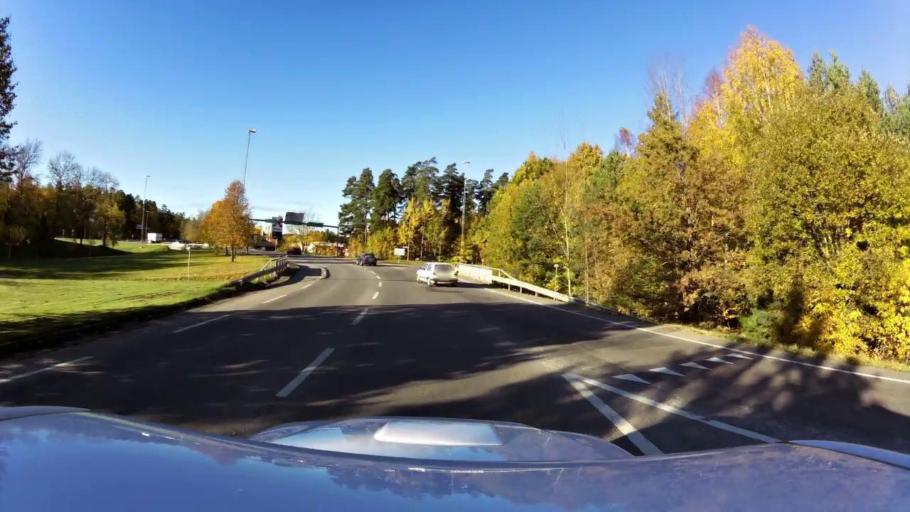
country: SE
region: OEstergoetland
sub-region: Linkopings Kommun
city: Linkoping
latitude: 58.4072
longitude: 15.5828
